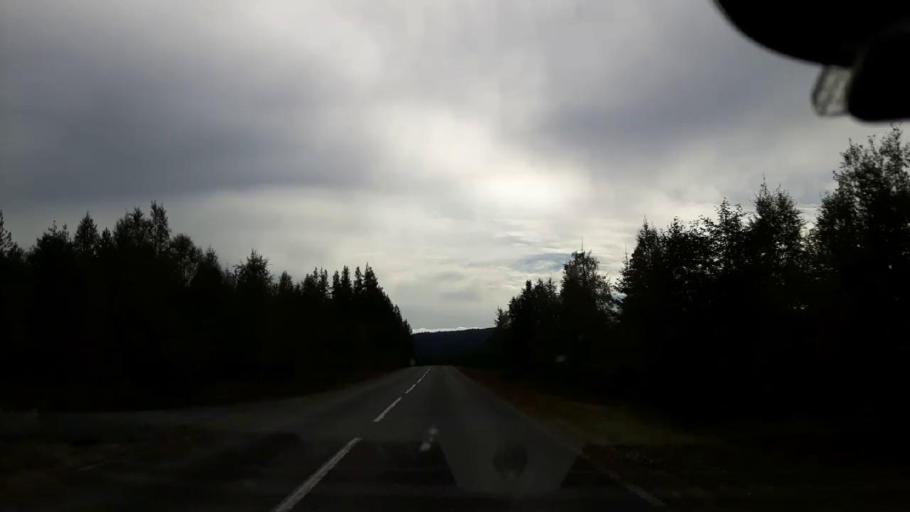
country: SE
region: Jaemtland
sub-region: Ragunda Kommun
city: Hammarstrand
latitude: 63.0504
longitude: 15.9274
